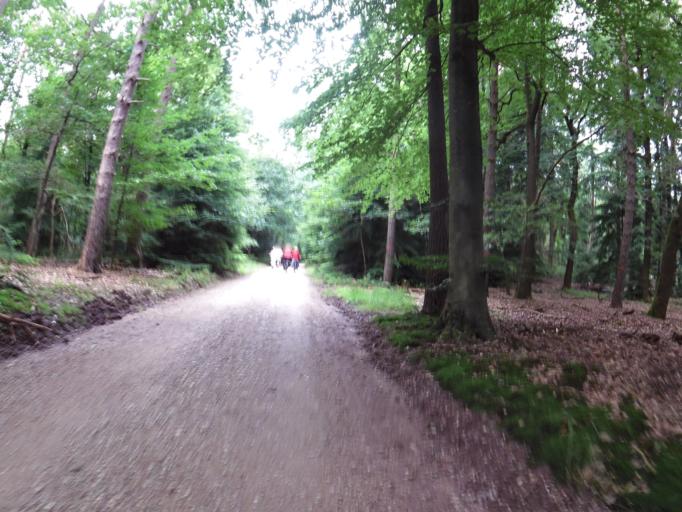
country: NL
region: Gelderland
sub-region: Gemeente Apeldoorn
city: Loenen
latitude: 52.1002
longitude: 6.0052
